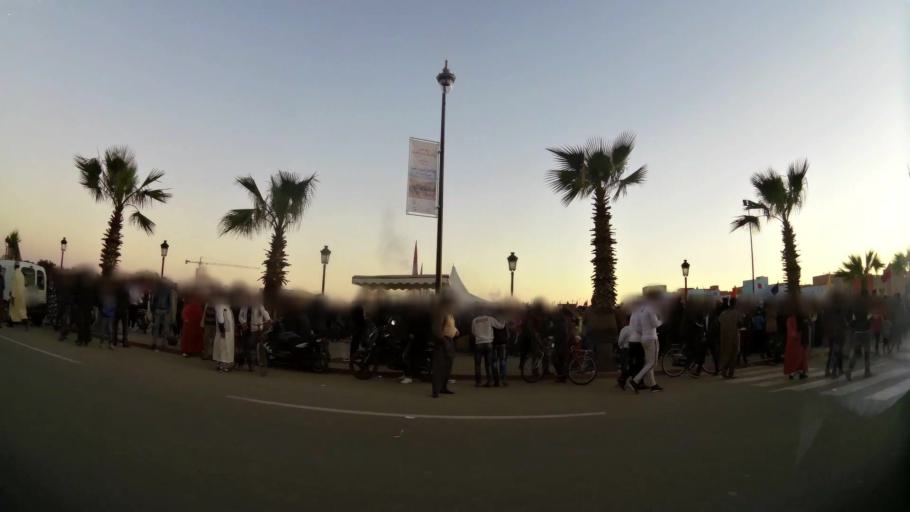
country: MA
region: Marrakech-Tensift-Al Haouz
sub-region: Kelaa-Des-Sraghna
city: Sidi Bou Othmane
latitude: 32.2272
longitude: -7.9450
